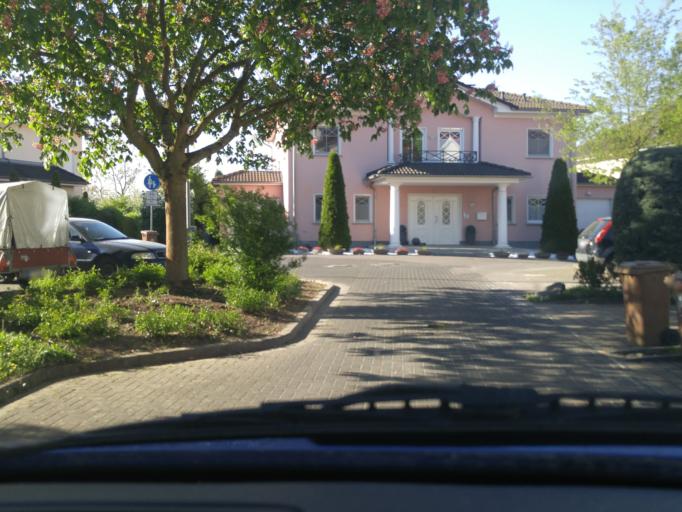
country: DE
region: Hesse
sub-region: Regierungsbezirk Darmstadt
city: Bad Nauheim
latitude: 50.3549
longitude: 8.7302
